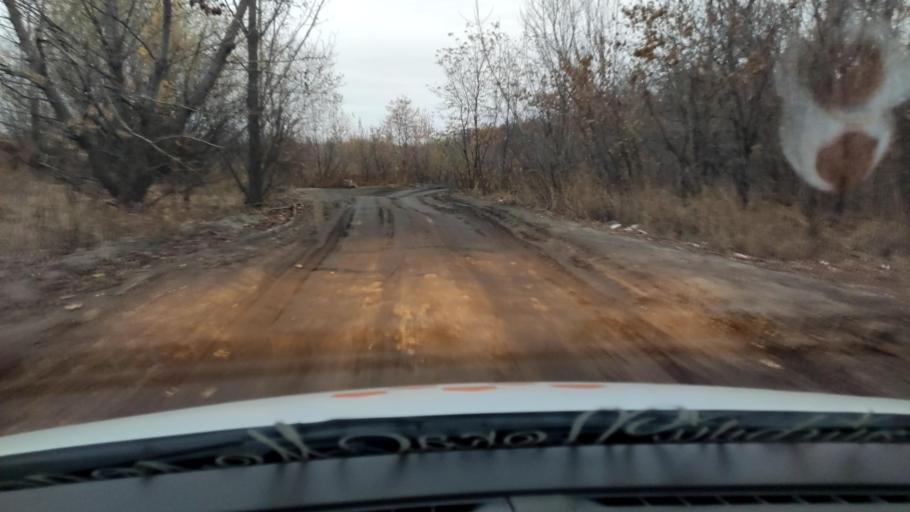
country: RU
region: Voronezj
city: Podgornoye
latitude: 51.7180
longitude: 39.1909
